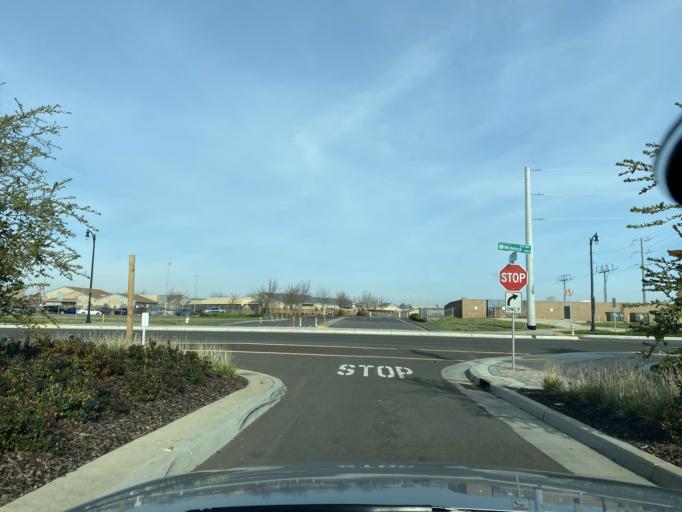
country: US
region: California
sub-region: Sacramento County
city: Elk Grove
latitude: 38.3942
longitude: -121.3957
